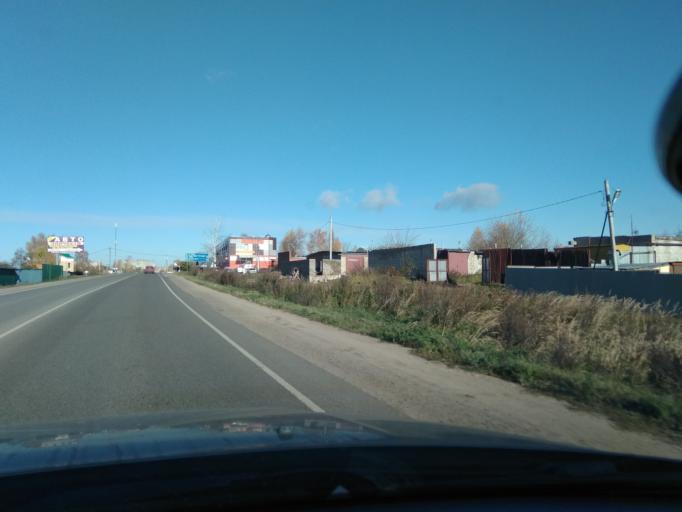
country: RU
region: Moskovskaya
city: Istra
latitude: 55.8959
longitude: 36.8620
